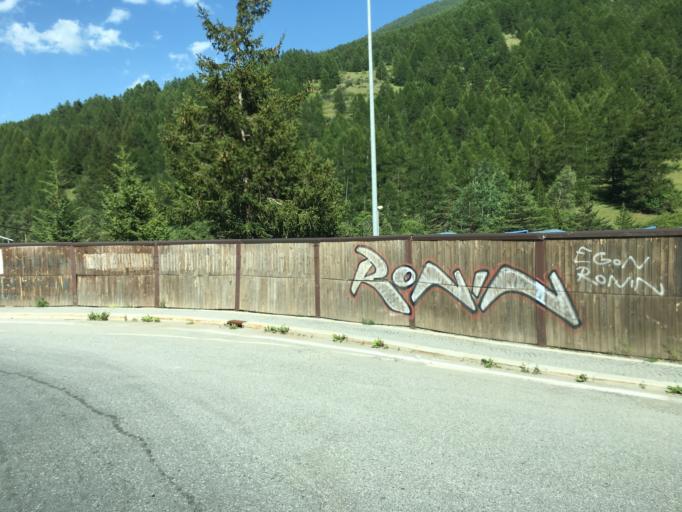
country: IT
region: Piedmont
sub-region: Provincia di Torino
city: Pragelato-Rua
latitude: 45.0192
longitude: 6.9472
